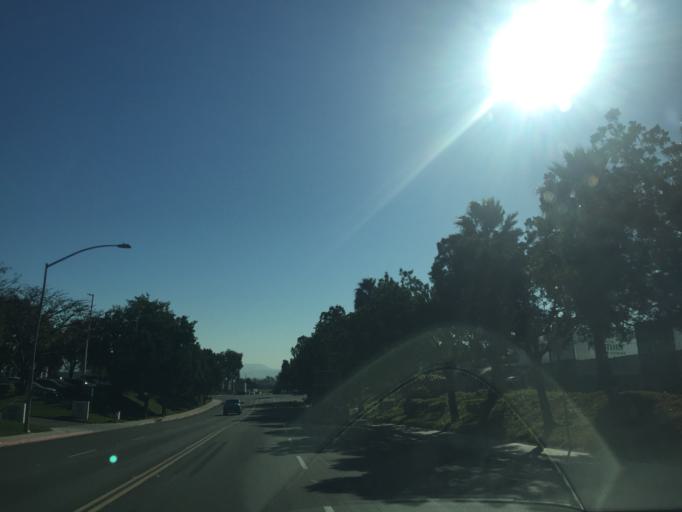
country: MX
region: Baja California
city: Tijuana
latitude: 32.5583
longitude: -116.9320
